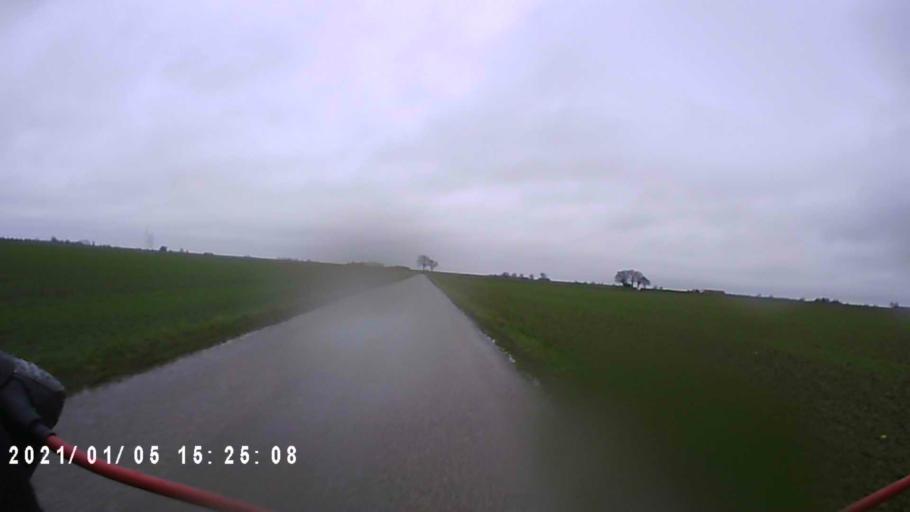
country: DE
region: Lower Saxony
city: Bunde
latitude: 53.2270
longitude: 7.1986
